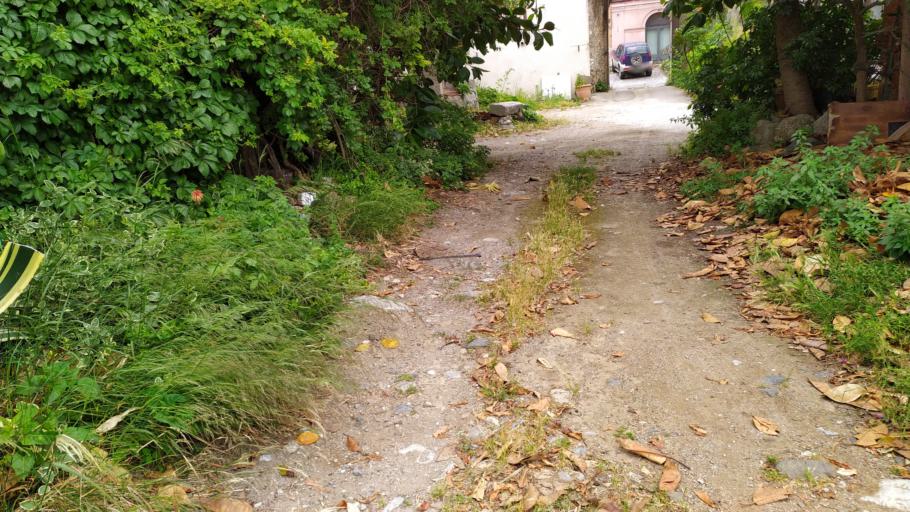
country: IT
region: Sicily
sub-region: Messina
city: San Filippo del Mela
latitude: 38.1794
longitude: 15.2651
